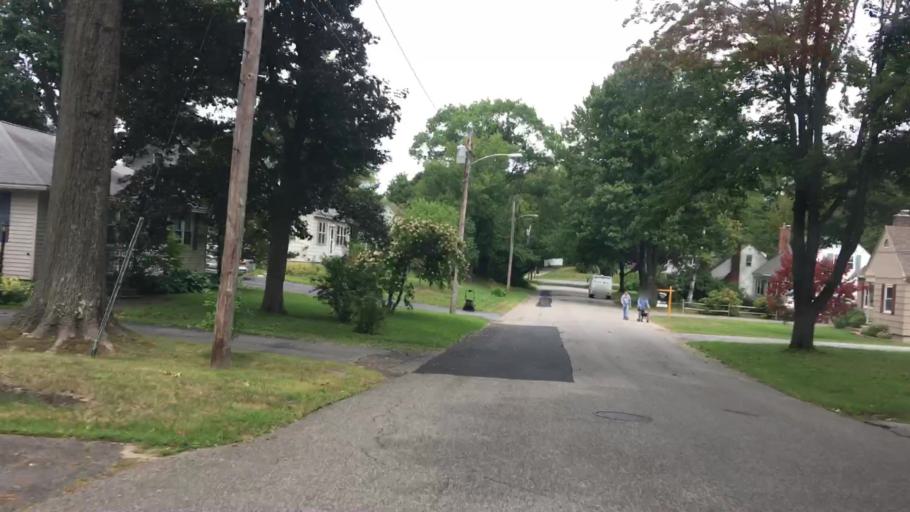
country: US
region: Maine
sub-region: Cumberland County
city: Westbrook
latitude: 43.6736
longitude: -70.3577
